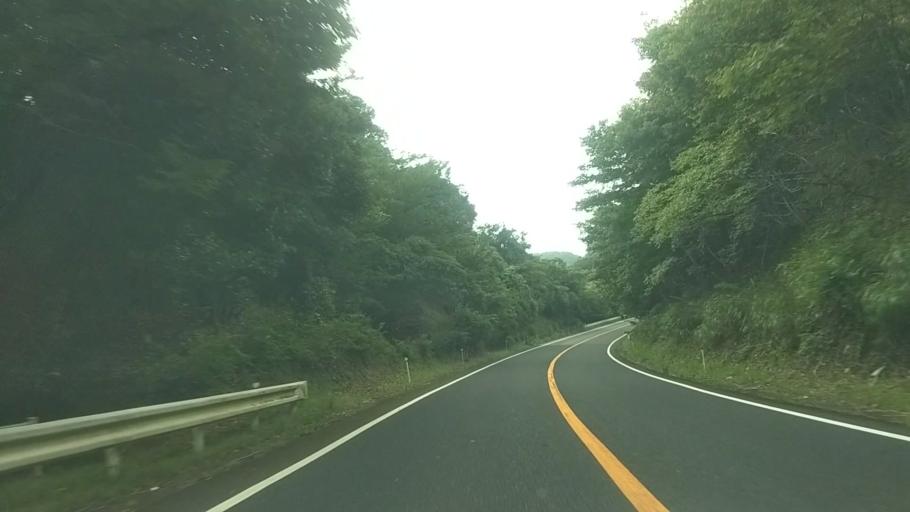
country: JP
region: Chiba
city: Kawaguchi
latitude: 35.2182
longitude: 140.0393
